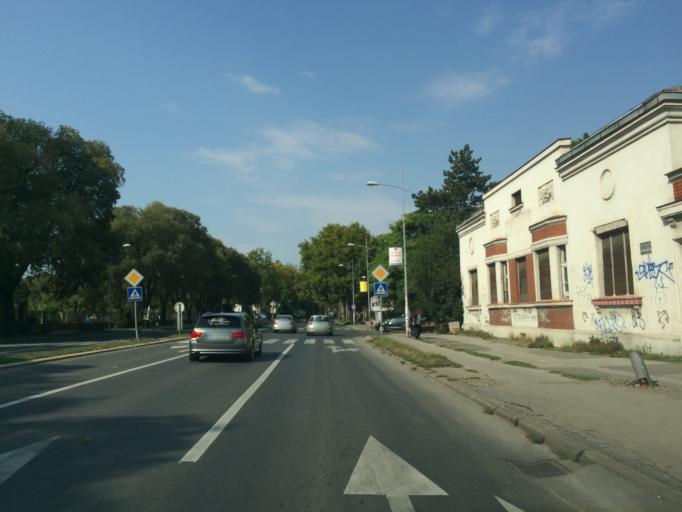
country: RS
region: Autonomna Pokrajina Vojvodina
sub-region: Juznobacki Okrug
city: Novi Sad
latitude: 45.2493
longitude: 19.8303
